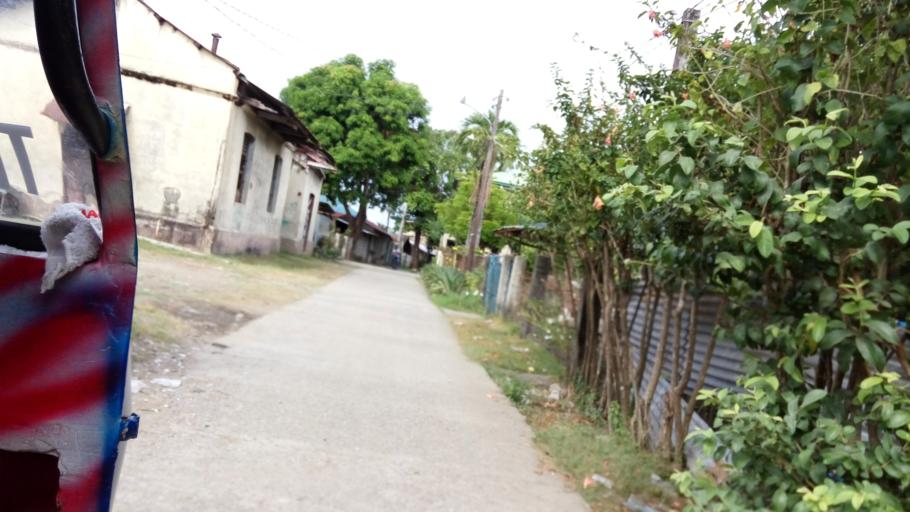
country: PH
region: Ilocos
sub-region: Province of La Union
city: Aringay
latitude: 16.3964
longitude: 120.3521
